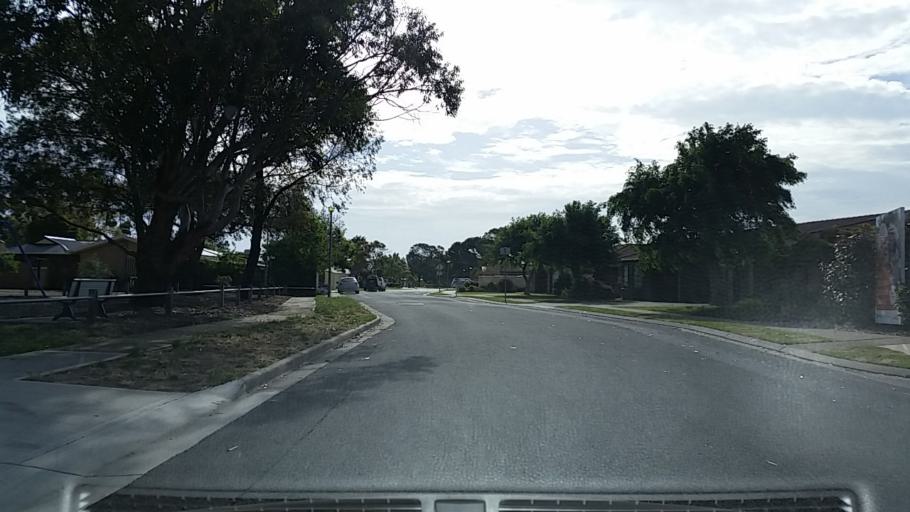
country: AU
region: South Australia
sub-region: Charles Sturt
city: Grange
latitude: -34.8971
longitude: 138.4990
